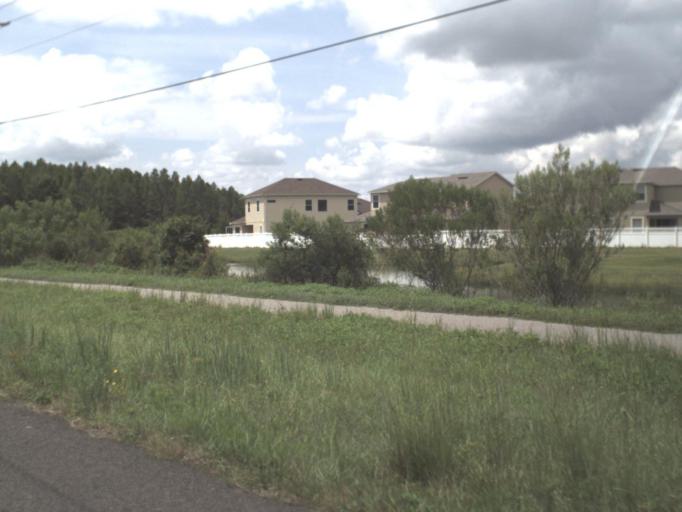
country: US
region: Florida
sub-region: Pasco County
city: Wesley Chapel
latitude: 28.2178
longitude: -82.3535
